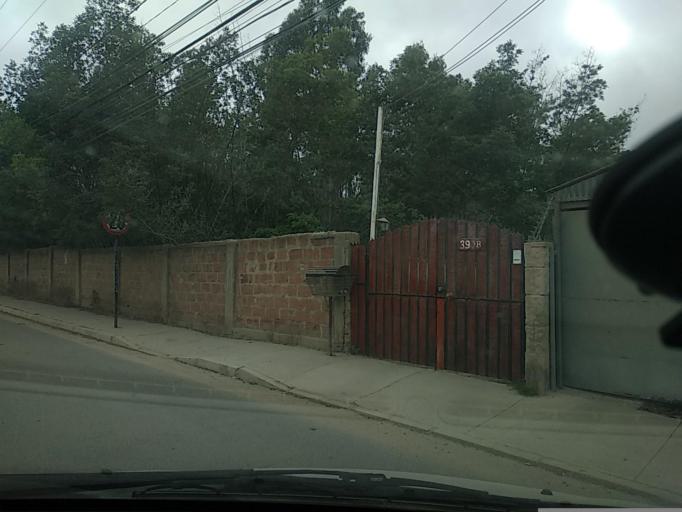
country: CL
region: Valparaiso
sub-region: Provincia de Marga Marga
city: Villa Alemana
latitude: -33.0381
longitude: -71.3588
